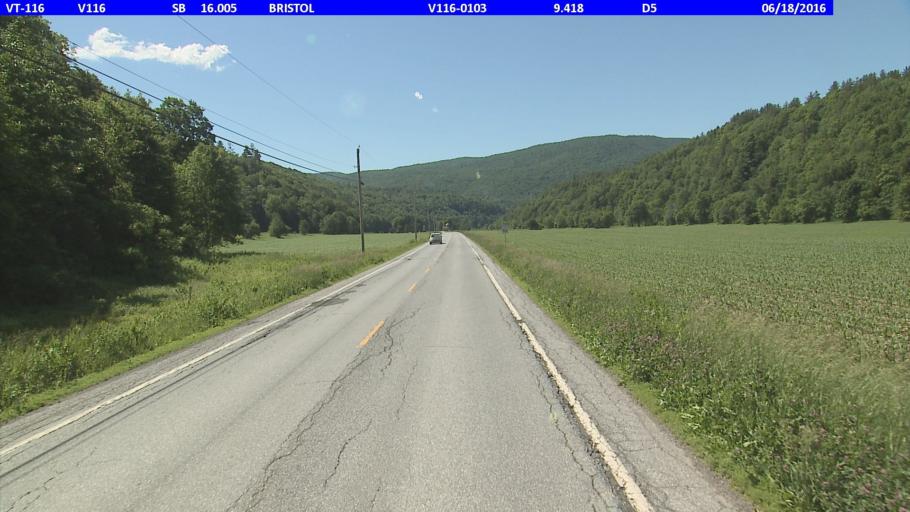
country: US
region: Vermont
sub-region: Addison County
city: Bristol
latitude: 44.1466
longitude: -73.0455
